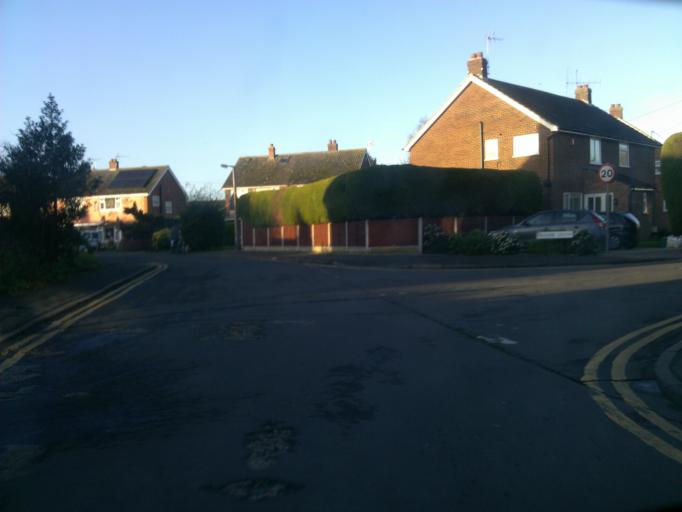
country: GB
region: England
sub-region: Essex
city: Wivenhoe
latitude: 51.8676
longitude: 0.9589
